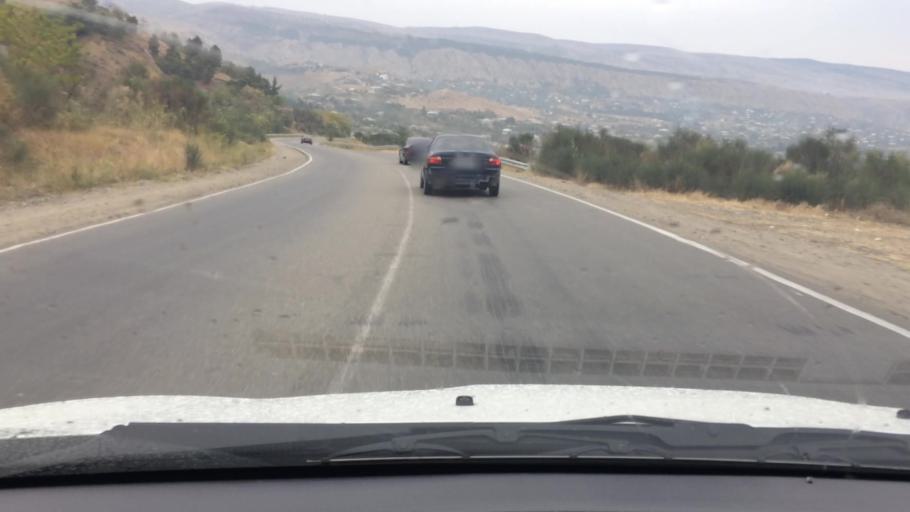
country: GE
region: T'bilisi
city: Tbilisi
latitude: 41.5937
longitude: 44.7805
